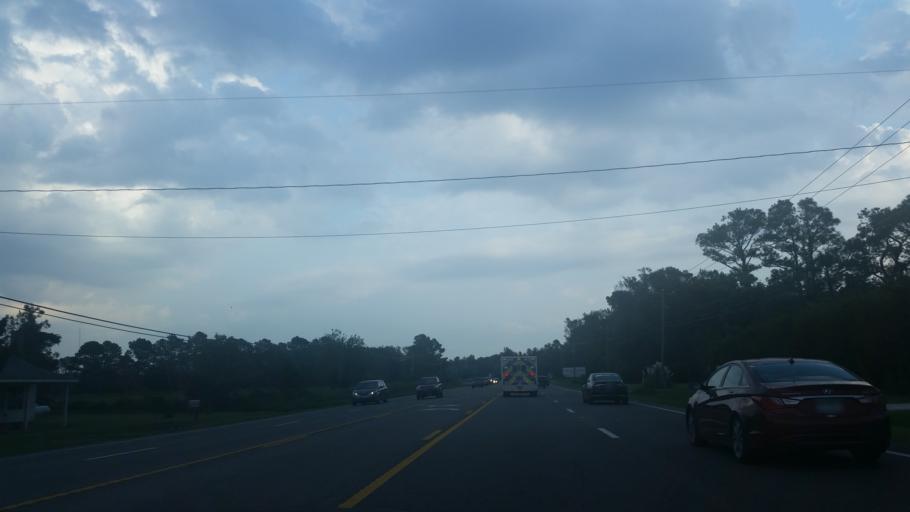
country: US
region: North Carolina
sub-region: Dare County
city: Southern Shores
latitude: 36.1565
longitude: -75.8580
